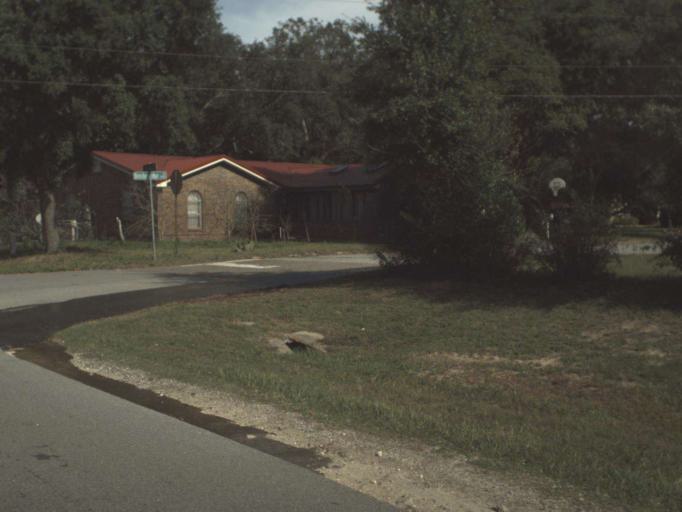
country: US
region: Florida
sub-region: Escambia County
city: Myrtle Grove
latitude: 30.4372
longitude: -87.3240
